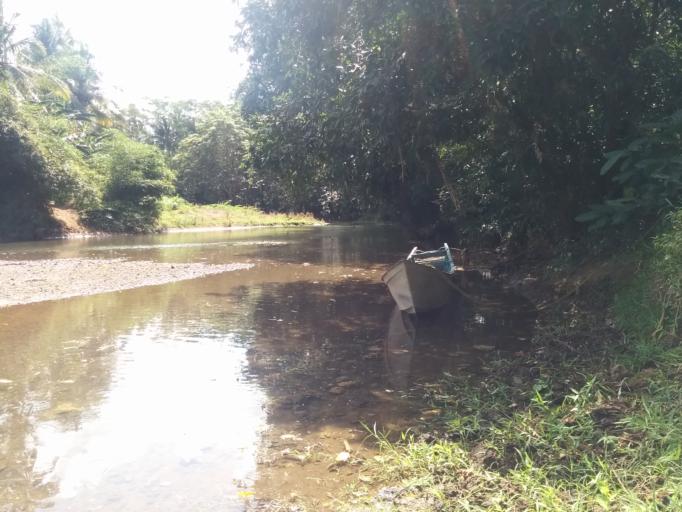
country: ID
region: East Java
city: Krajan Sidodadi
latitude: -8.4096
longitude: 112.6514
